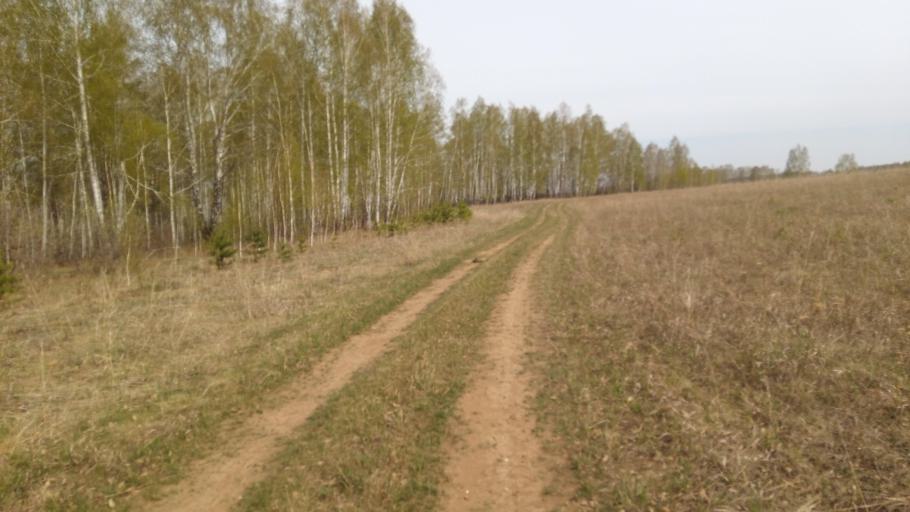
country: RU
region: Chelyabinsk
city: Timiryazevskiy
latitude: 55.0218
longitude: 60.8588
